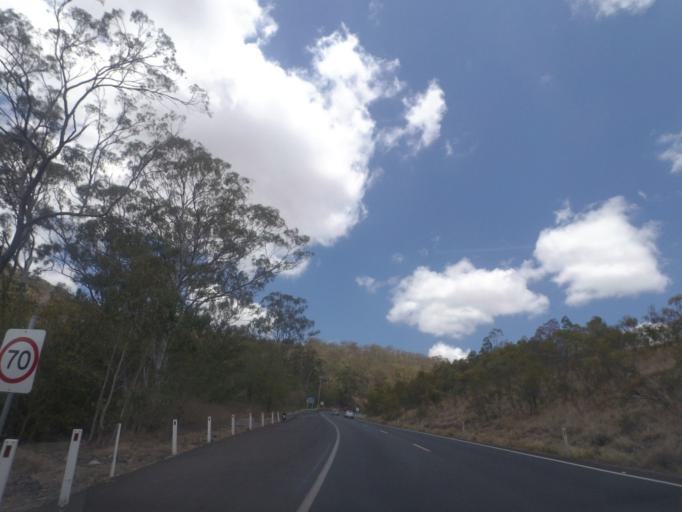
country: AU
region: Queensland
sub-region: Toowoomba
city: East Toowoomba
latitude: -27.5718
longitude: 151.9864
